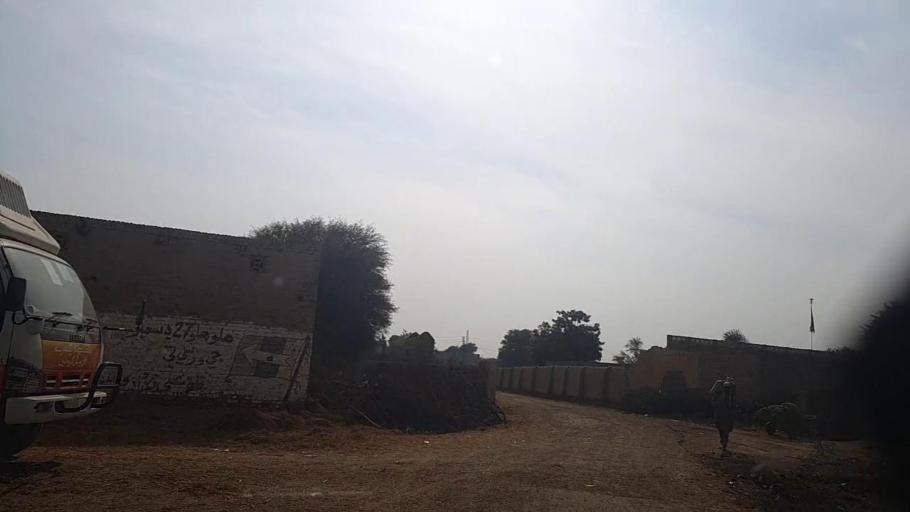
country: PK
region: Sindh
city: Daur
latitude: 26.4028
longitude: 68.2389
